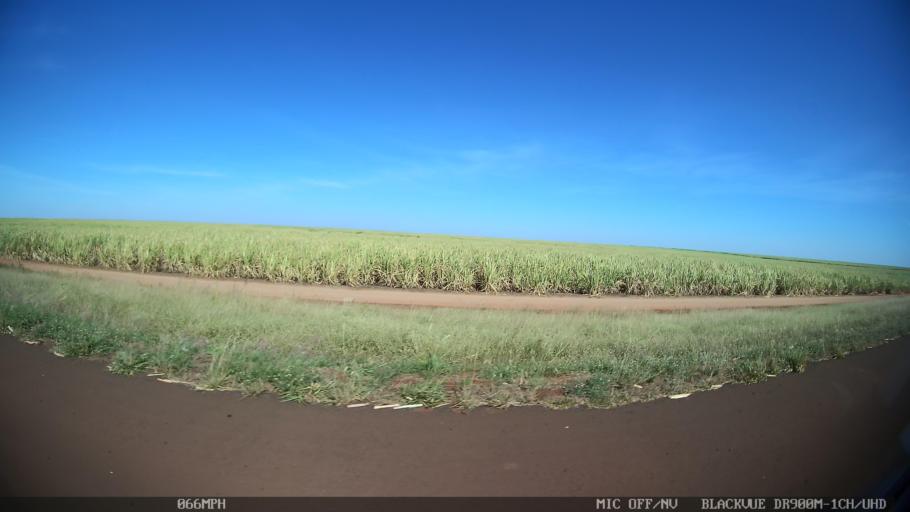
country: BR
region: Sao Paulo
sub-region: Guaira
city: Guaira
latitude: -20.4449
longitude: -48.2520
